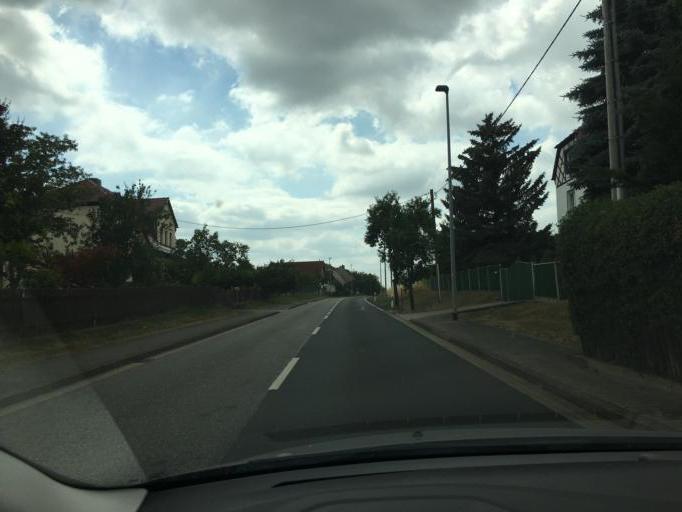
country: DE
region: Saxony
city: Kitzscher
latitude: 51.1244
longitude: 12.5849
